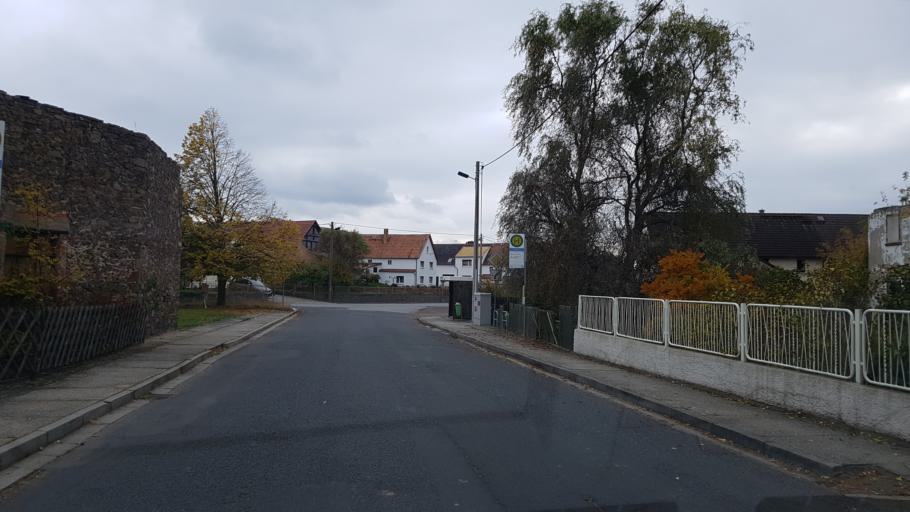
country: DE
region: Saxony
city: Dahlen
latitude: 51.3832
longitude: 12.9481
